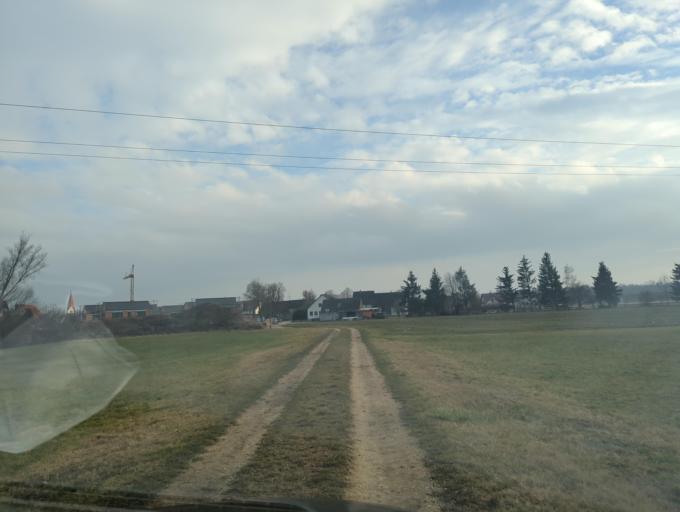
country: DE
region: Bavaria
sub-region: Swabia
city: Leipheim
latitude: 48.4626
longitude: 10.1836
